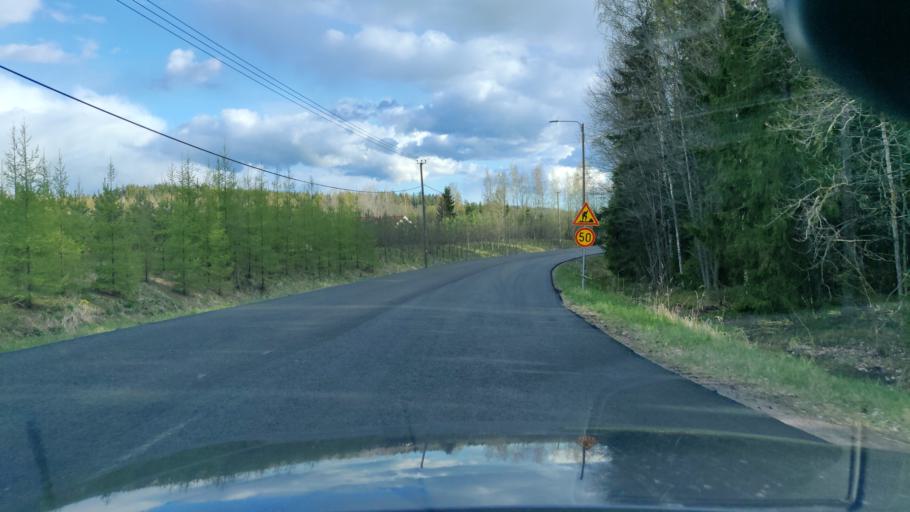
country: FI
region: Uusimaa
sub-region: Helsinki
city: Nurmijaervi
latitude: 60.3625
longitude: 24.7248
